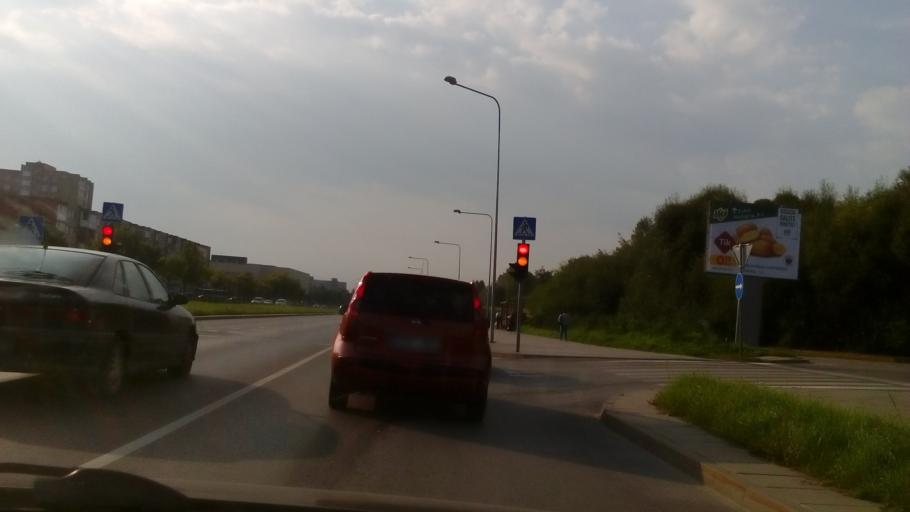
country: LT
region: Alytaus apskritis
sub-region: Alytus
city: Alytus
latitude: 54.4070
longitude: 24.0181
